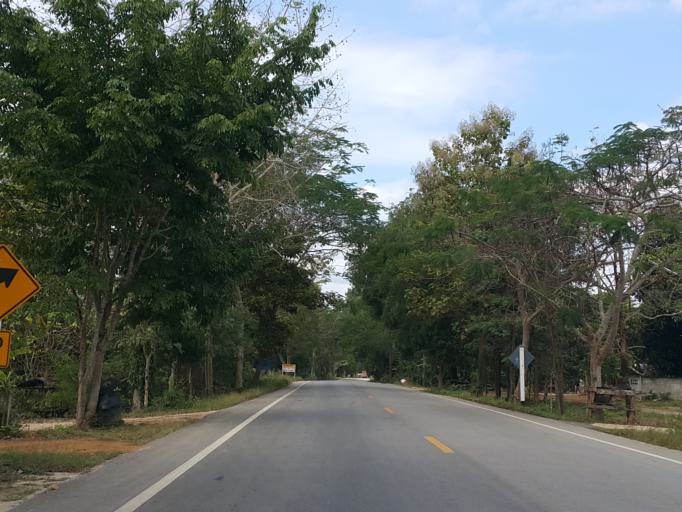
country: TH
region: Lampang
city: Lampang
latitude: 18.4199
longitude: 99.4469
